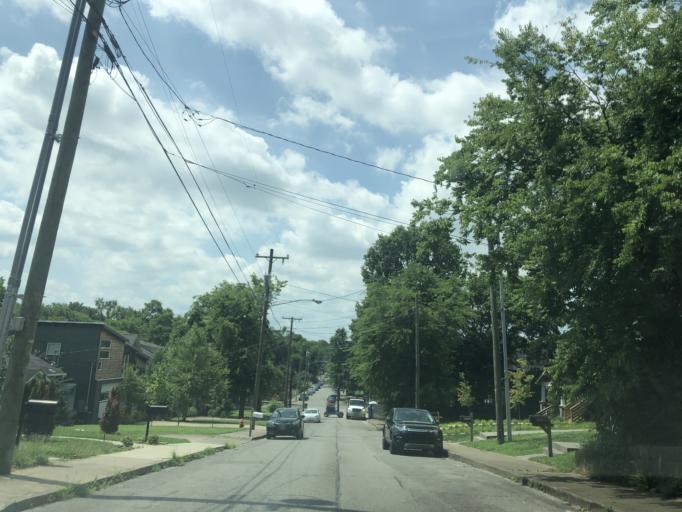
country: US
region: Tennessee
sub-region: Davidson County
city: Nashville
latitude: 36.1949
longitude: -86.7644
